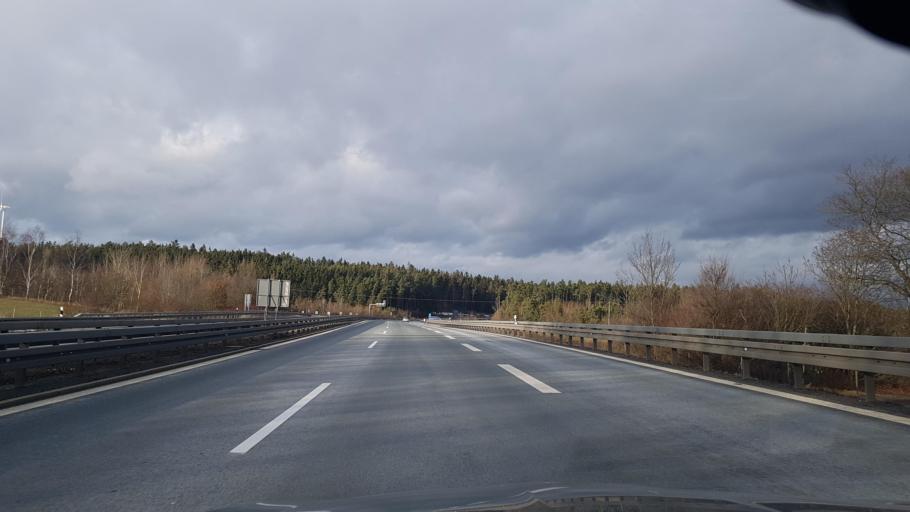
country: DE
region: Bavaria
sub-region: Upper Franconia
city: Thiersheim
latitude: 50.0736
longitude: 12.1018
